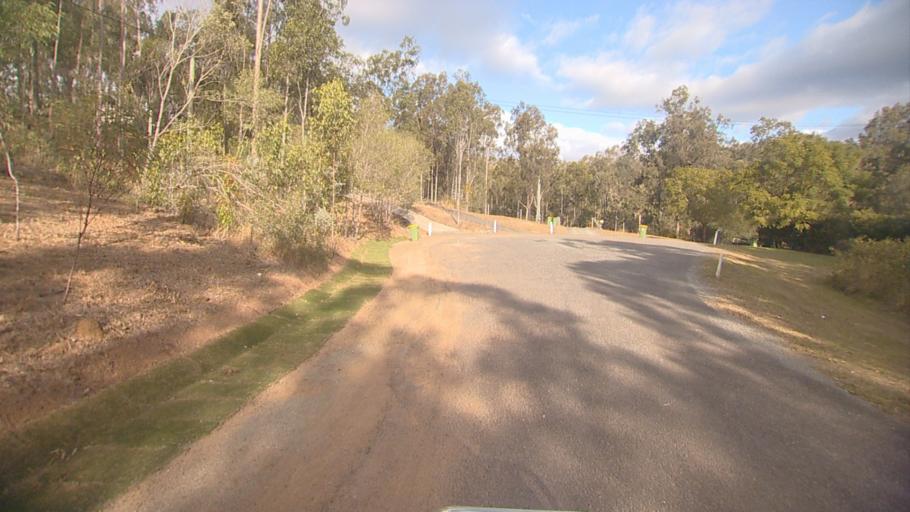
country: AU
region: Queensland
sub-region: Logan
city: Cedar Vale
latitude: -27.9080
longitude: 153.0641
